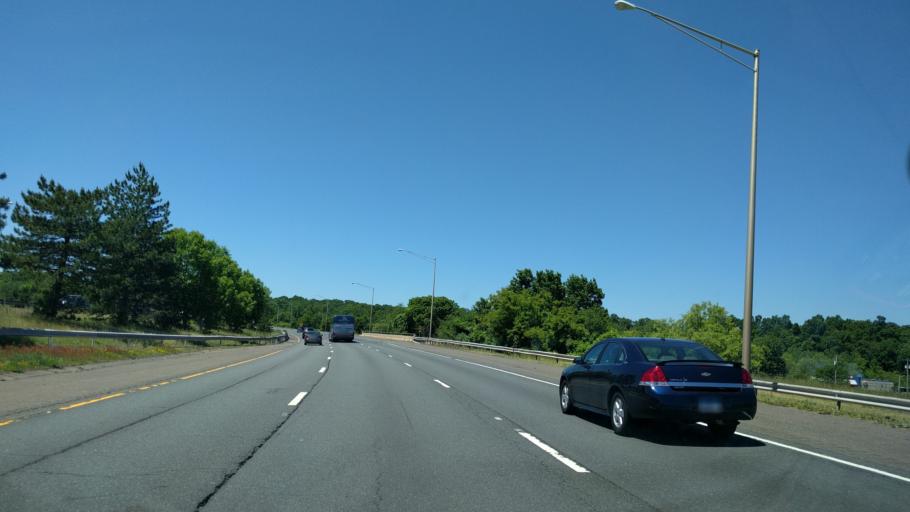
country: US
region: Connecticut
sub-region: Tolland County
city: Rockville
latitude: 41.8551
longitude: -72.4277
